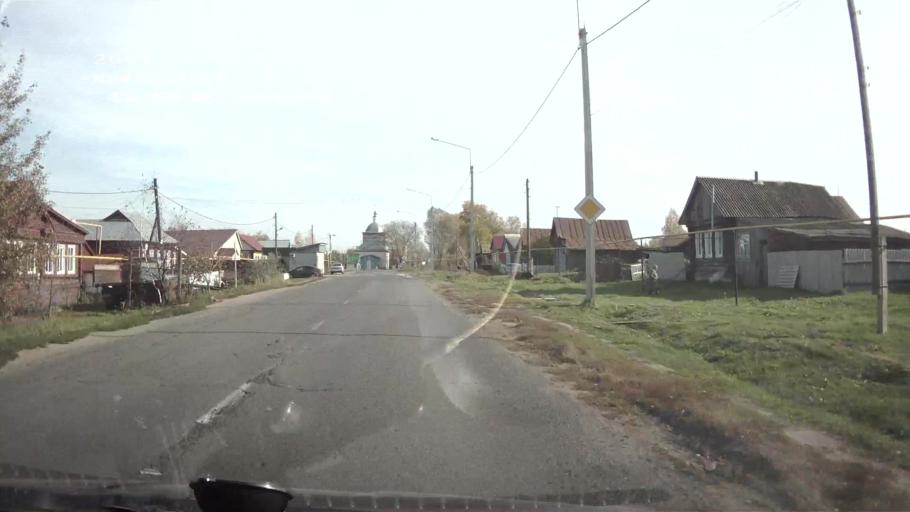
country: RU
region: Mordoviya
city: Turgenevo
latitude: 54.8547
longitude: 46.4060
